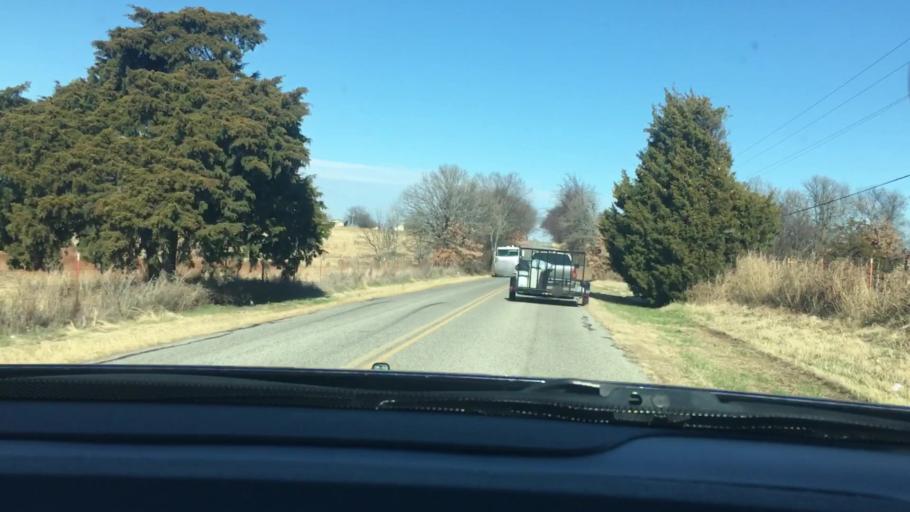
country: US
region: Oklahoma
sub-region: Murray County
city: Davis
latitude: 34.4872
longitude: -97.0555
